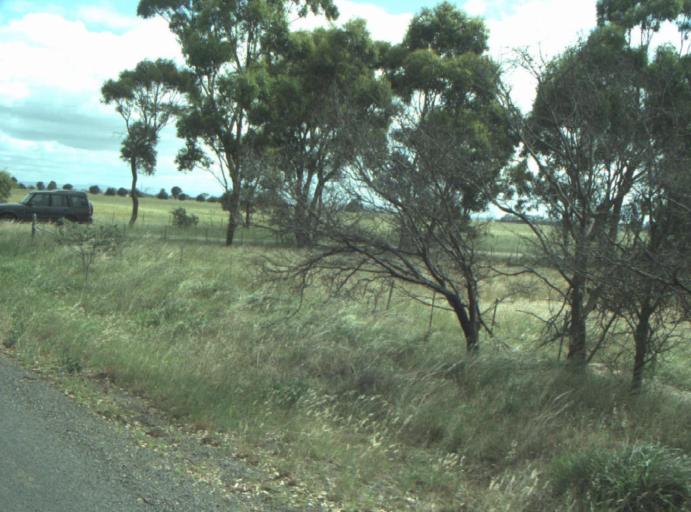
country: AU
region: Victoria
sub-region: Greater Geelong
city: Lara
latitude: -37.8706
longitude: 144.3501
